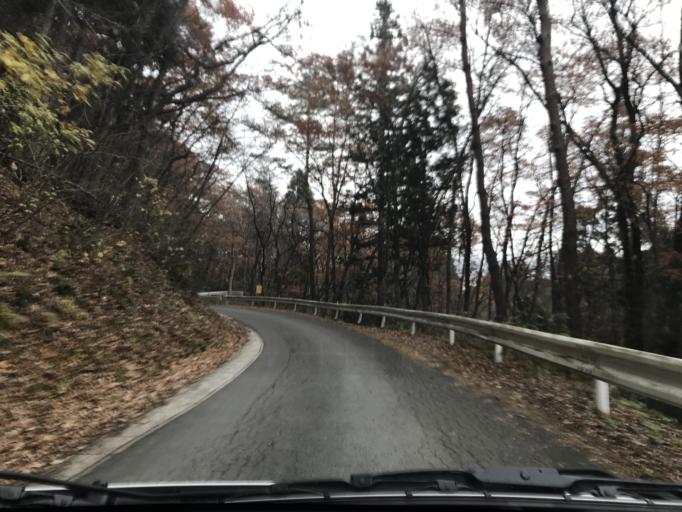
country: JP
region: Iwate
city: Ichinoseki
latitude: 38.9786
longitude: 140.9987
